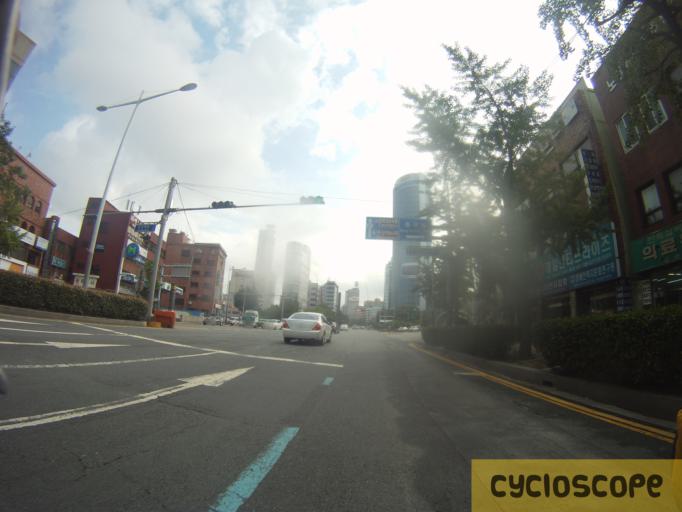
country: KR
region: Busan
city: Busan
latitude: 35.1249
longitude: 129.0458
